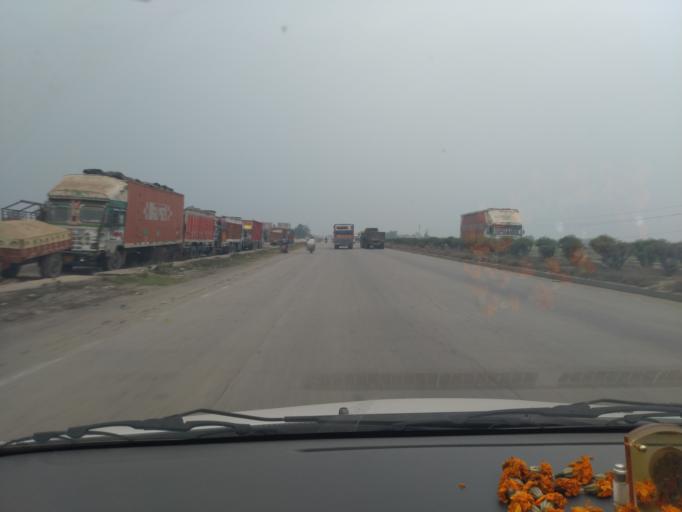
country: IN
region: Bihar
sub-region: Rohtas
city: Dehri
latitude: 24.9737
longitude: 83.9069
